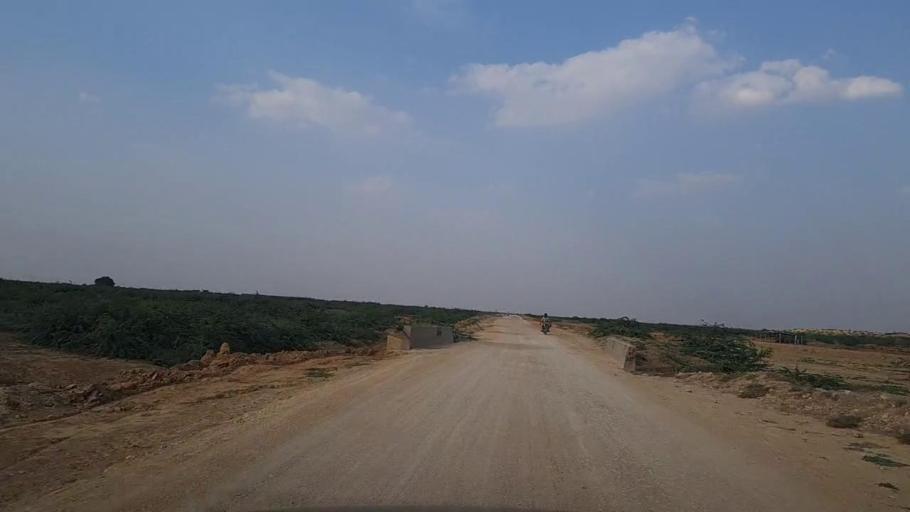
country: PK
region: Sindh
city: Gharo
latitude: 24.8170
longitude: 67.7429
